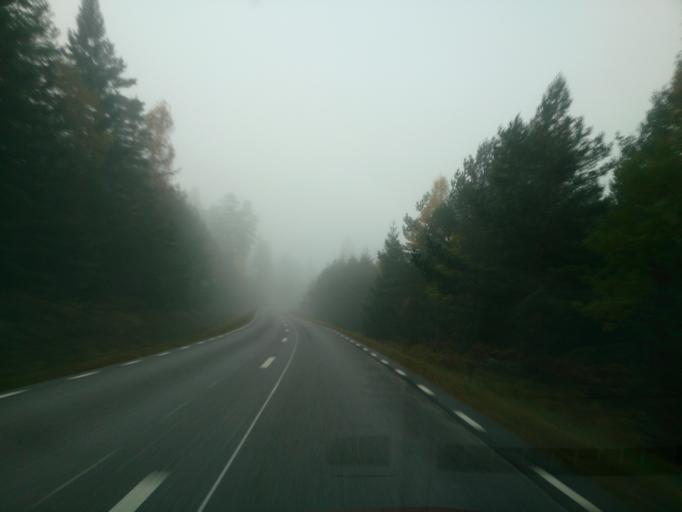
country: SE
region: OEstergoetland
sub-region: Atvidabergs Kommun
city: Atvidaberg
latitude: 58.1111
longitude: 15.9510
